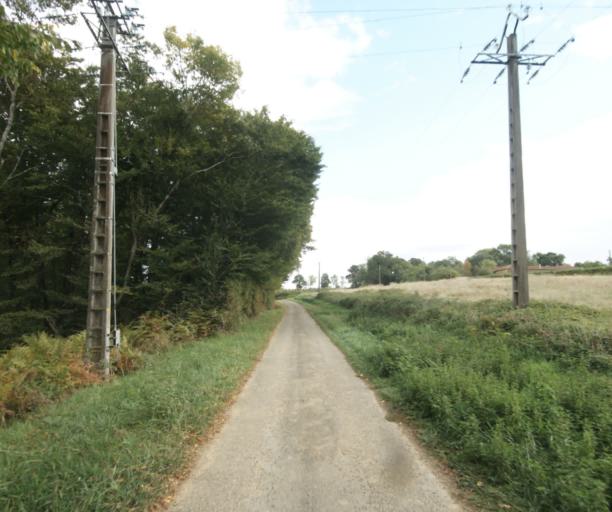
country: FR
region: Midi-Pyrenees
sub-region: Departement du Gers
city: Eauze
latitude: 43.8523
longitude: 0.0512
